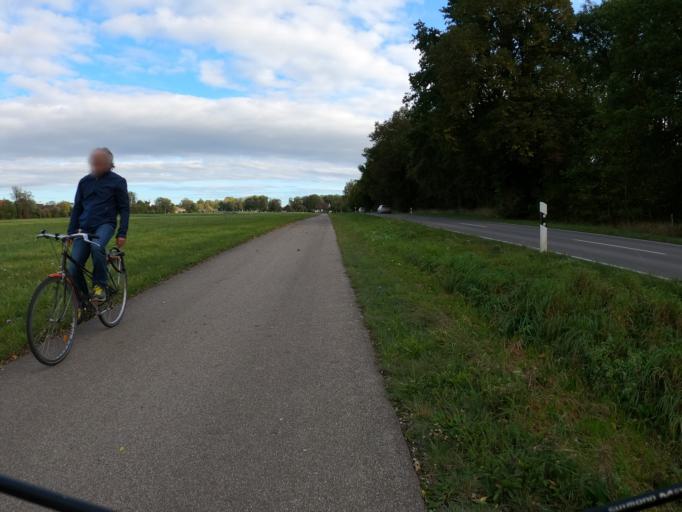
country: DE
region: Bavaria
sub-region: Swabia
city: Holzheim
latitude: 48.4001
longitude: 10.0963
